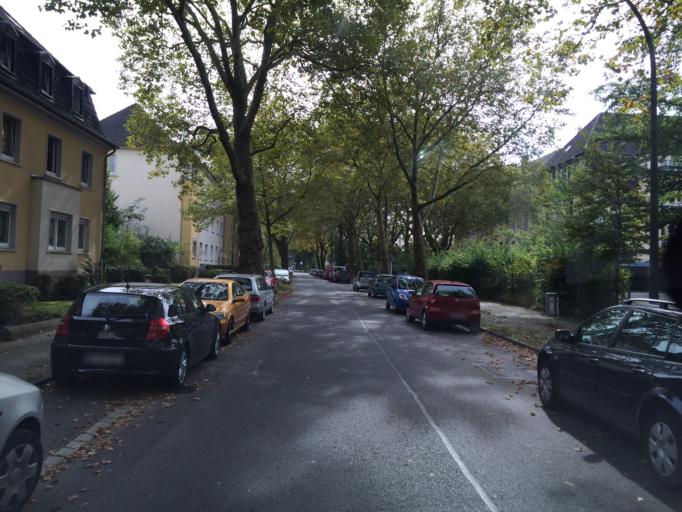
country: DE
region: North Rhine-Westphalia
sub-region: Regierungsbezirk Arnsberg
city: Dortmund
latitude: 51.4844
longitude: 7.4904
